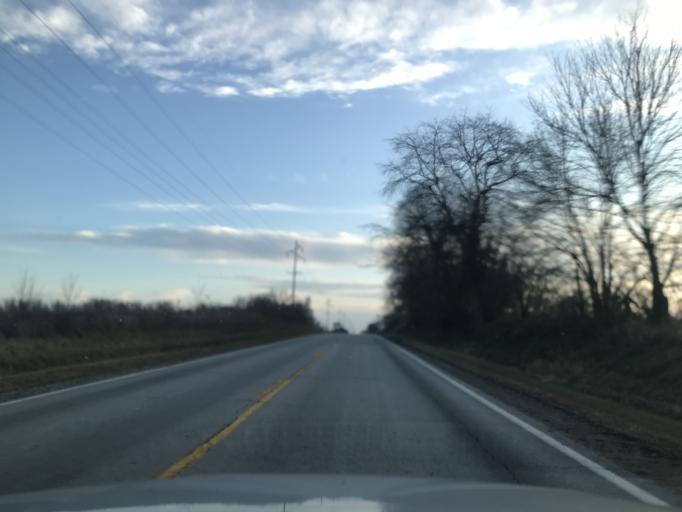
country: US
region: Illinois
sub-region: Mercer County
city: Aledo
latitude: 41.0409
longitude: -90.7459
